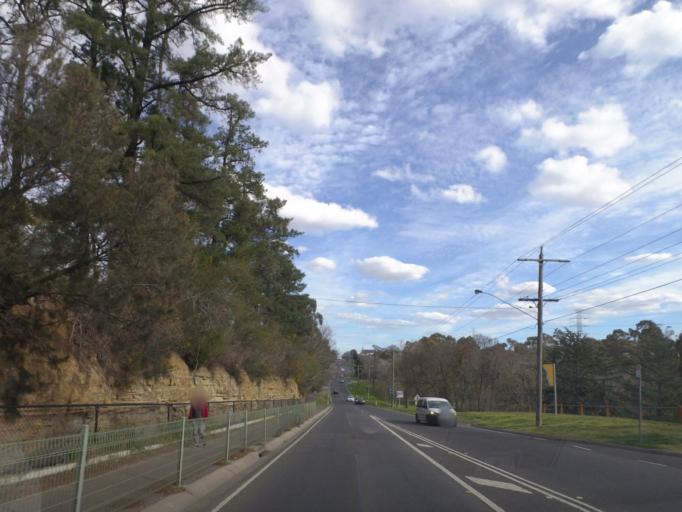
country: AU
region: Victoria
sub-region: Manningham
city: Doncaster East
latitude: -37.7777
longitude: 145.1453
